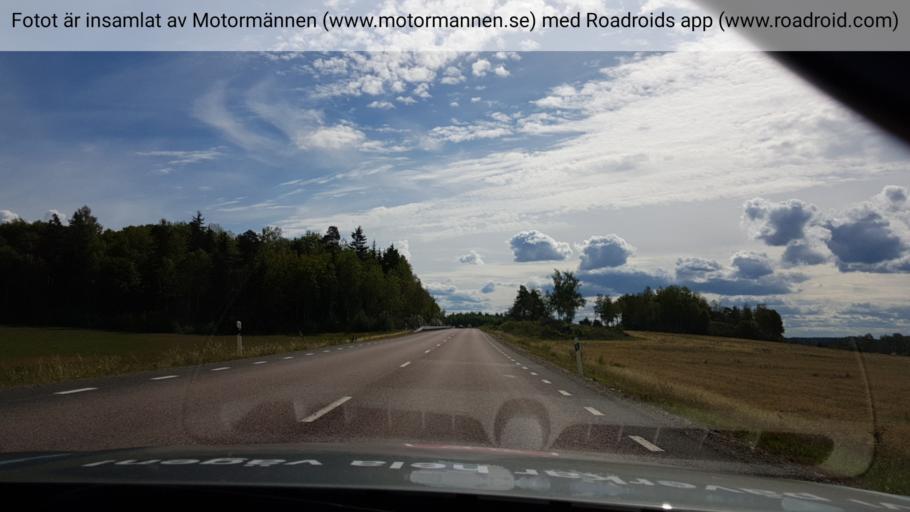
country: SE
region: Uppsala
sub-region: Osthammars Kommun
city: Bjorklinge
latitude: 59.9424
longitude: 17.4360
